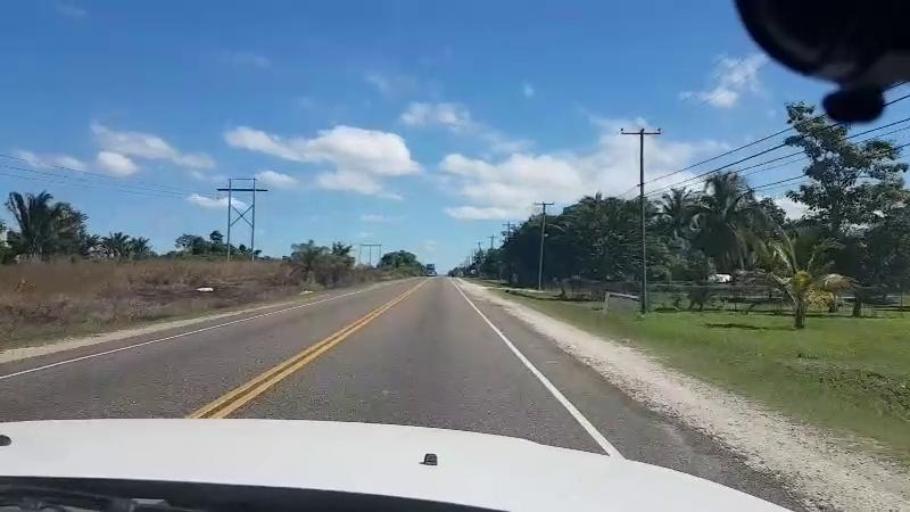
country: BZ
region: Cayo
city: Belmopan
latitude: 17.2768
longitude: -88.7178
